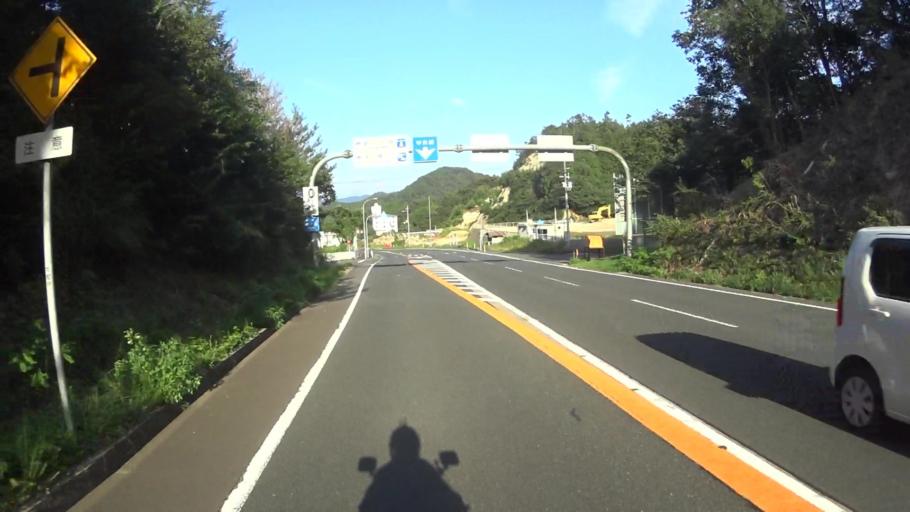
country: JP
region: Hyogo
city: Toyooka
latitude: 35.5941
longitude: 134.8780
